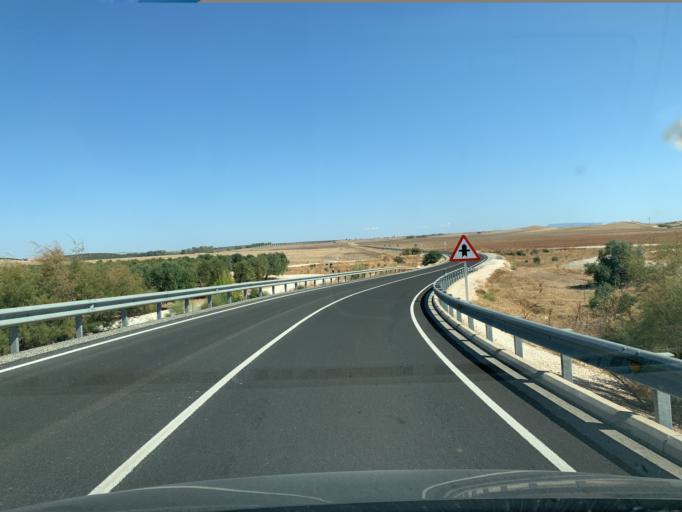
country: ES
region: Andalusia
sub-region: Provincia de Sevilla
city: Marchena
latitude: 37.3251
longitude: -5.3445
